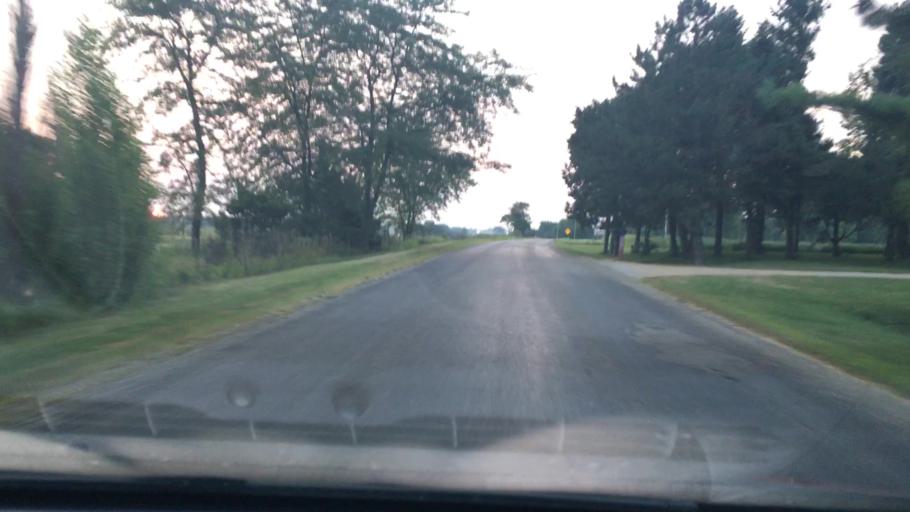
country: US
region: Illinois
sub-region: Bureau County
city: Ladd
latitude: 41.3643
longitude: -89.2015
